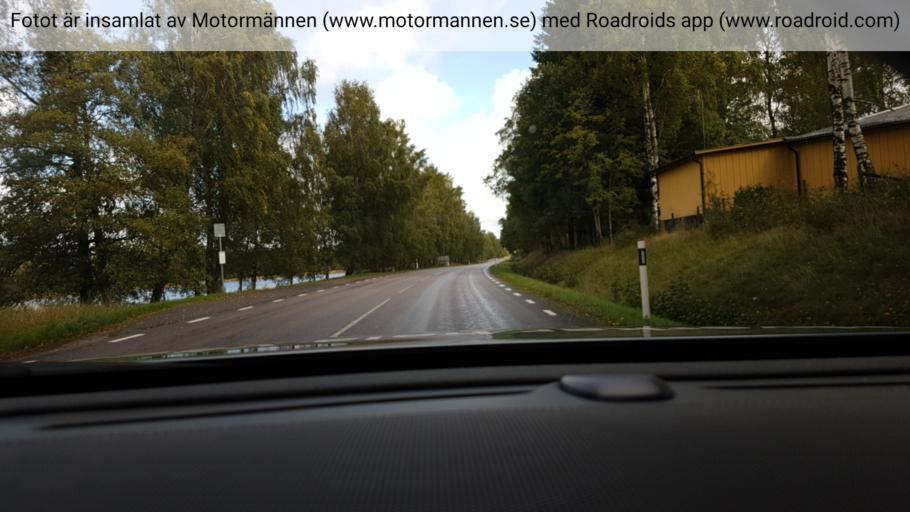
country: SE
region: Vaestra Goetaland
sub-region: Svenljunga Kommun
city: Svenljunga
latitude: 57.4093
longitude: 12.9654
